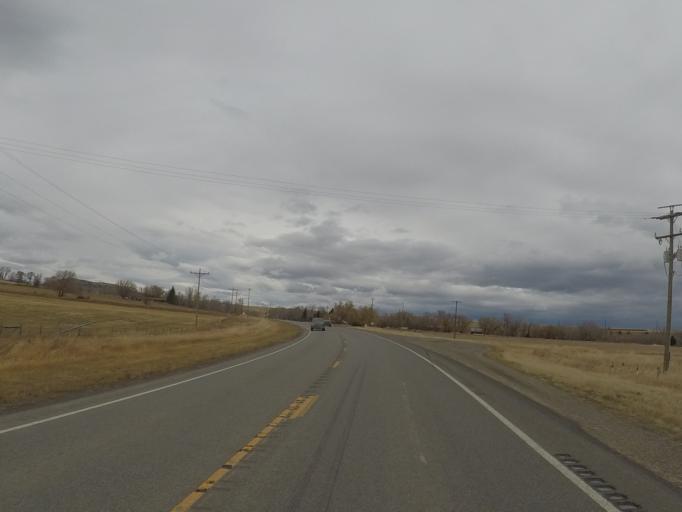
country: US
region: Montana
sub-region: Sweet Grass County
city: Big Timber
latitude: 45.8514
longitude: -109.9399
